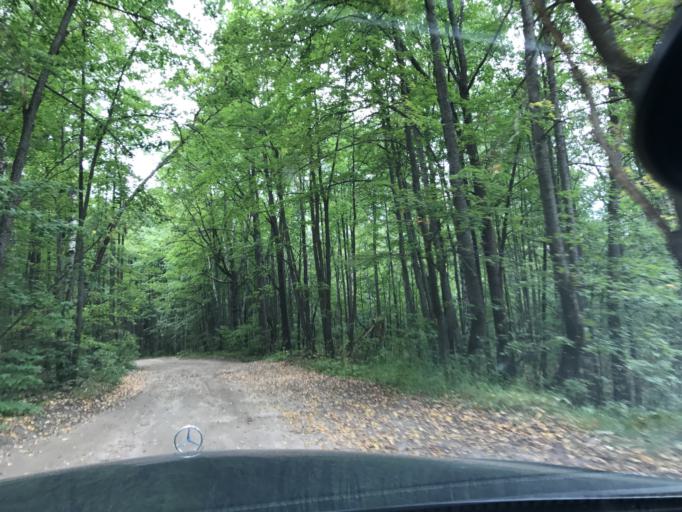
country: RU
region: Nizjnij Novgorod
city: Vacha
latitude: 55.9891
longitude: 42.8111
